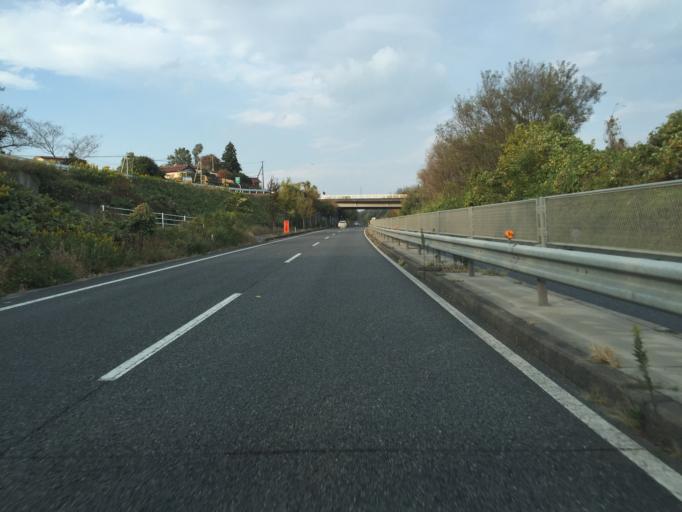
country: JP
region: Fukushima
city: Nihommatsu
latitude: 37.6526
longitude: 140.4886
